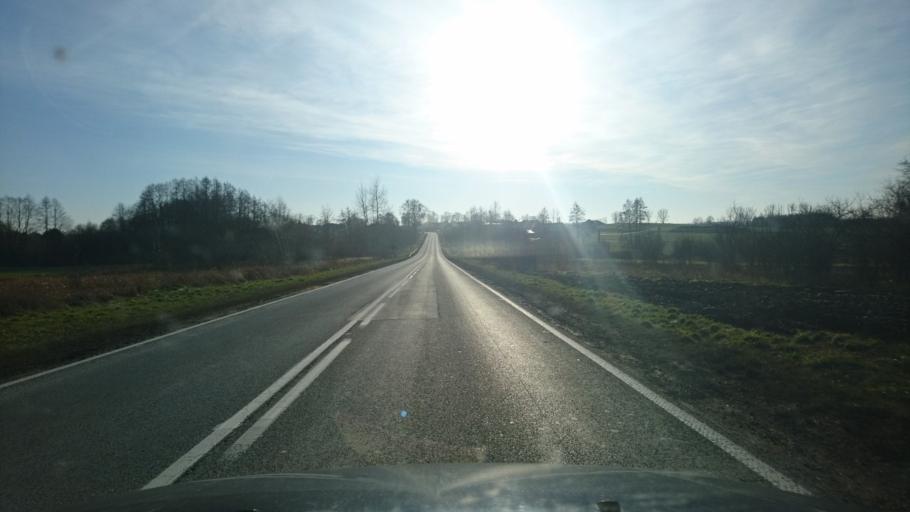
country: PL
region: Opole Voivodeship
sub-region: Powiat oleski
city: Dalachow
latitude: 51.0479
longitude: 18.5974
